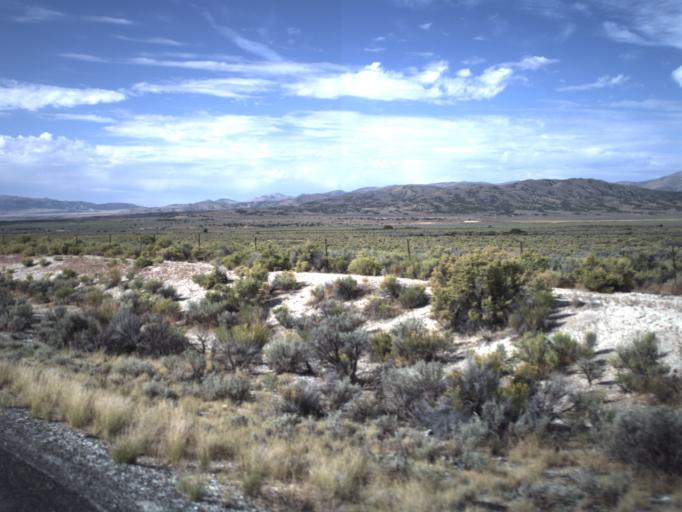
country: US
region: Idaho
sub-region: Cassia County
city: Burley
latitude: 41.6839
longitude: -113.5396
